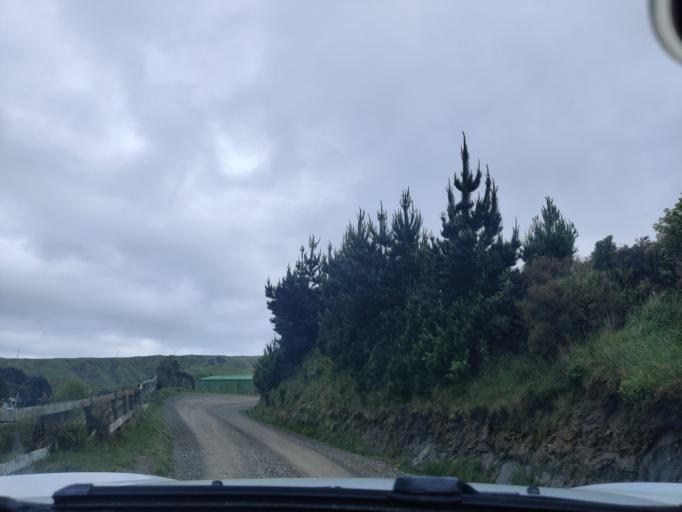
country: NZ
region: Manawatu-Wanganui
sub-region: Palmerston North City
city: Palmerston North
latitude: -40.2872
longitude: 175.8608
